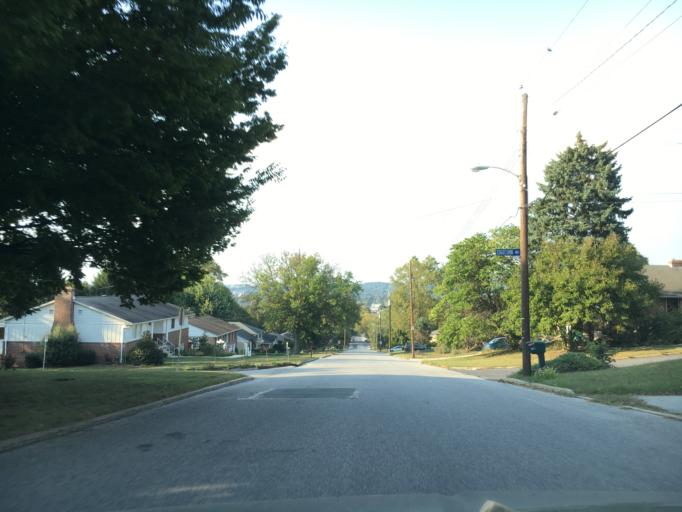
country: US
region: Pennsylvania
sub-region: York County
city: Valley View
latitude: 39.9519
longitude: -76.6992
